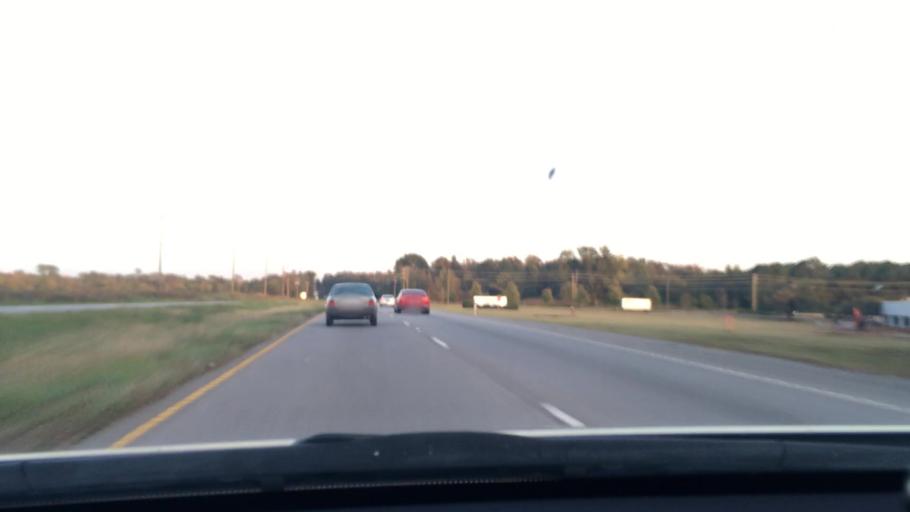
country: US
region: South Carolina
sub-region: Richland County
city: Hopkins
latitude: 33.9445
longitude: -80.8843
